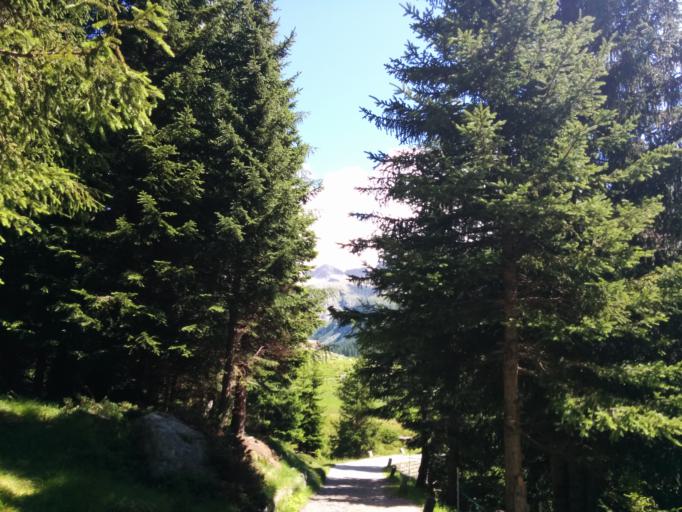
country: IT
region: Lombardy
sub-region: Provincia di Brescia
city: Saviore
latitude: 46.0708
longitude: 10.5380
